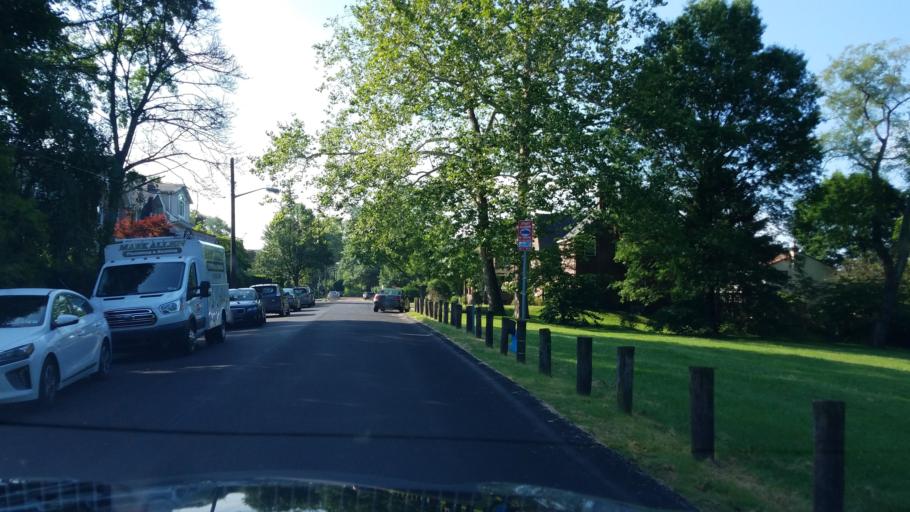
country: US
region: Pennsylvania
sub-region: Allegheny County
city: Edgewood
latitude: 40.4343
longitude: -79.8976
